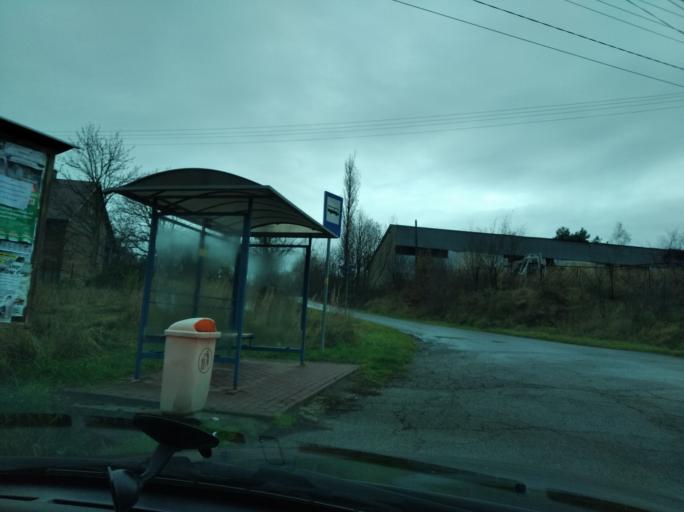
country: PL
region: Subcarpathian Voivodeship
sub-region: Powiat rzeszowski
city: Lecka
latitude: 49.9103
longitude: 22.0216
